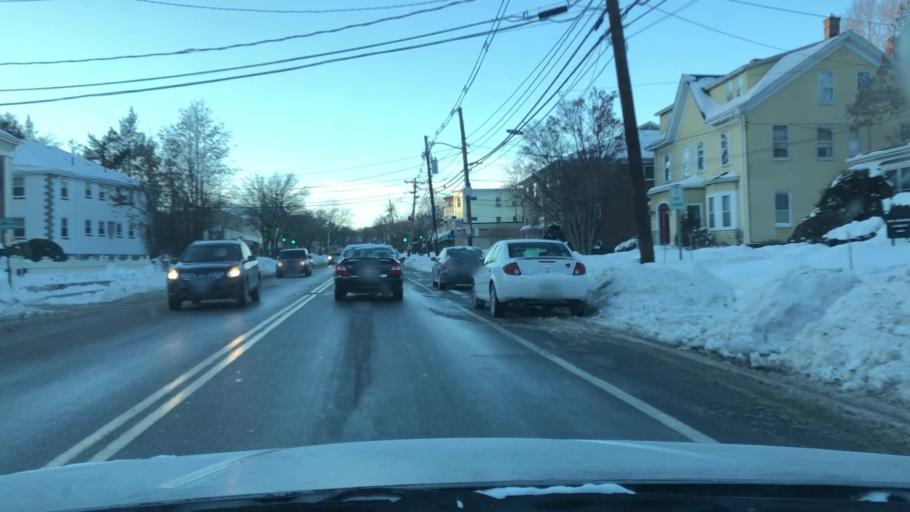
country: US
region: Massachusetts
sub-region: Middlesex County
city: Arlington
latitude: 42.4200
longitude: -71.1690
